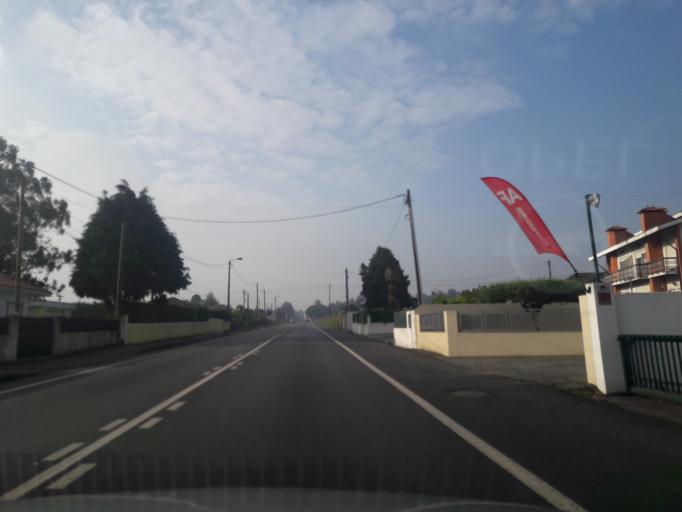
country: PT
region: Porto
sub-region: Vila do Conde
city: Arvore
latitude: 41.3128
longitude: -8.7075
